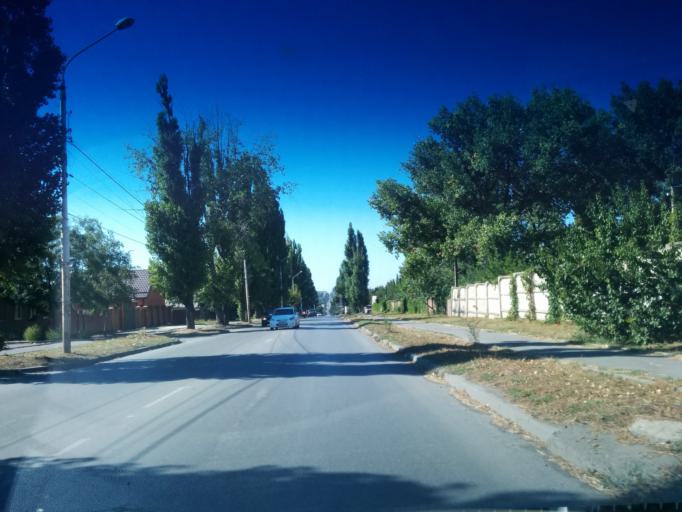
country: RU
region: Rostov
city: Shakhty
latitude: 47.6932
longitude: 40.2481
